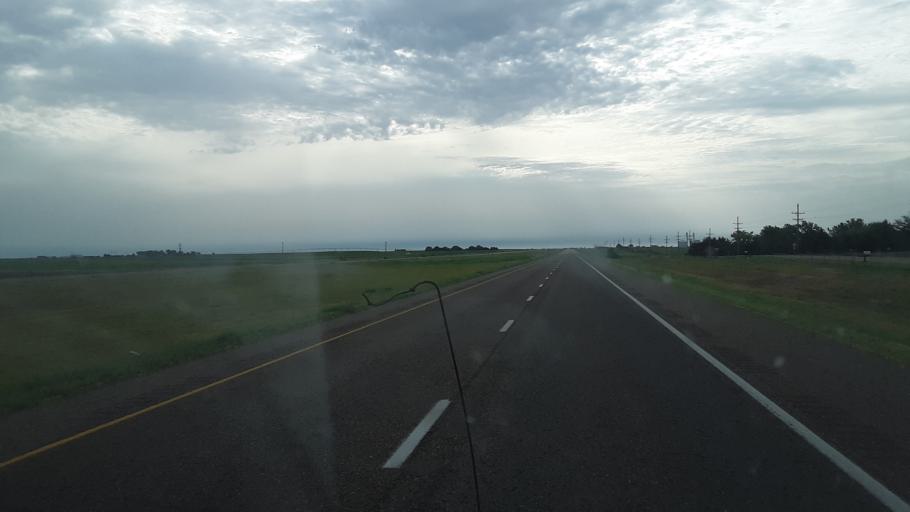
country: US
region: Kansas
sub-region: Finney County
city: Garden City
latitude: 37.9605
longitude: -100.7702
